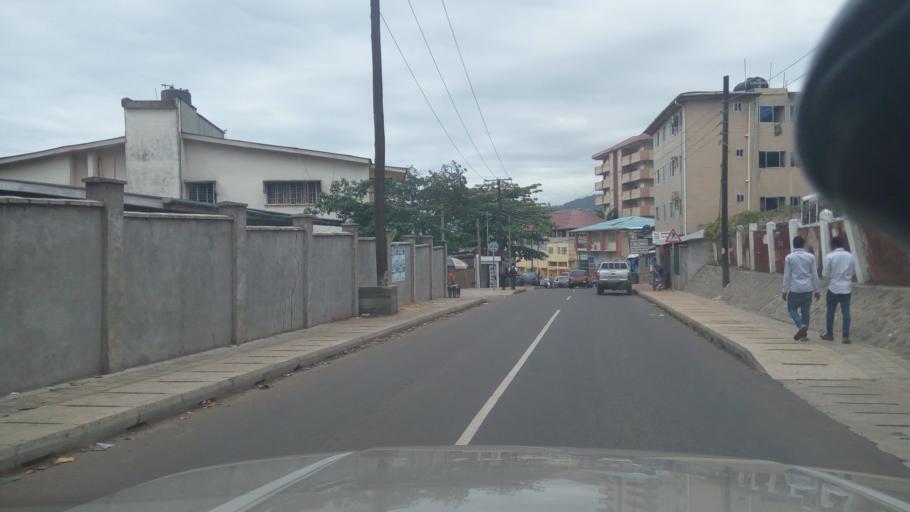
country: SL
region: Western Area
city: Freetown
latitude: 8.4830
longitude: -13.2605
